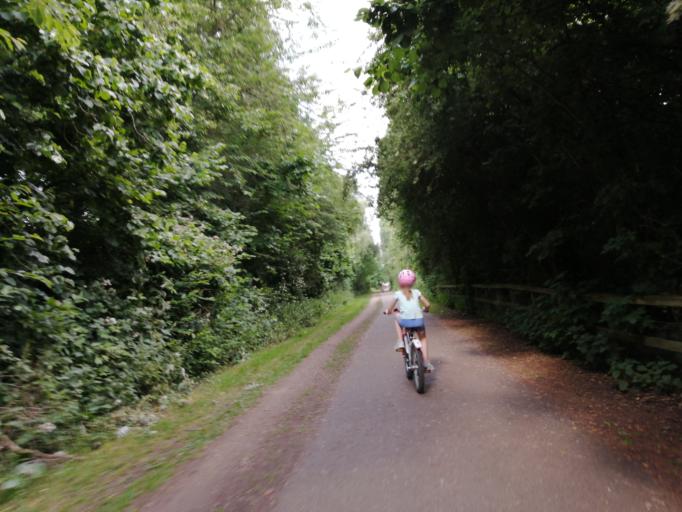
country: GB
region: England
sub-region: Peterborough
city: Peterborough
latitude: 52.5584
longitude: -0.2884
